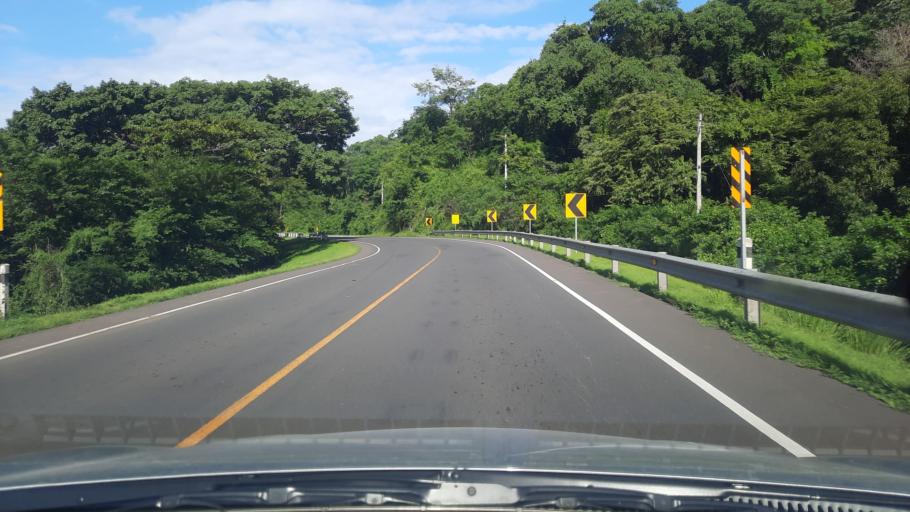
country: NI
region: Leon
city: Telica
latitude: 12.6953
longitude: -86.8624
